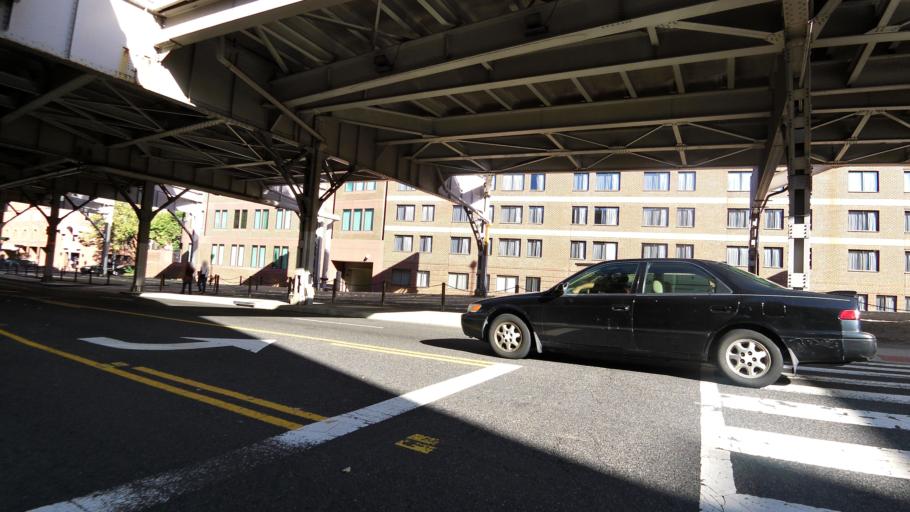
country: US
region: Washington, D.C.
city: Washington, D.C.
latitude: 38.9024
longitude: -77.0582
